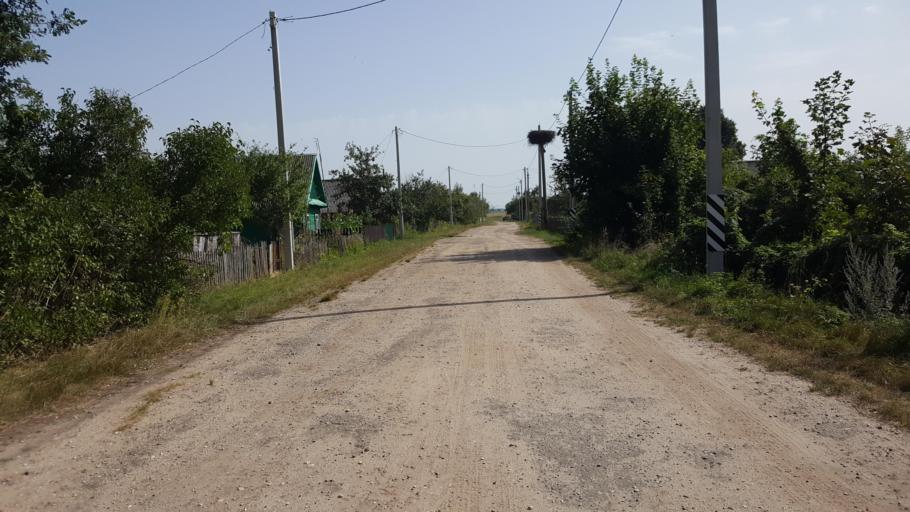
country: BY
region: Brest
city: Pruzhany
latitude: 52.4916
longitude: 24.6136
